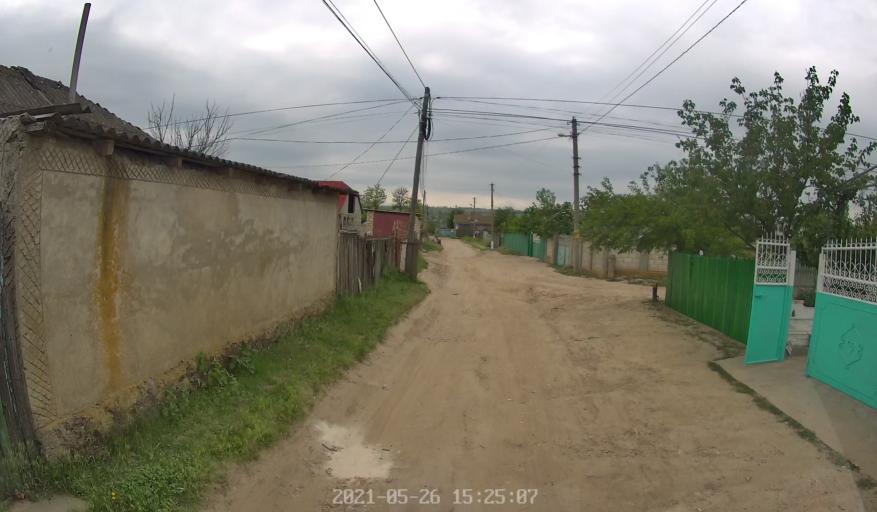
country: MD
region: Hincesti
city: Dancu
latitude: 46.6661
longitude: 28.3217
